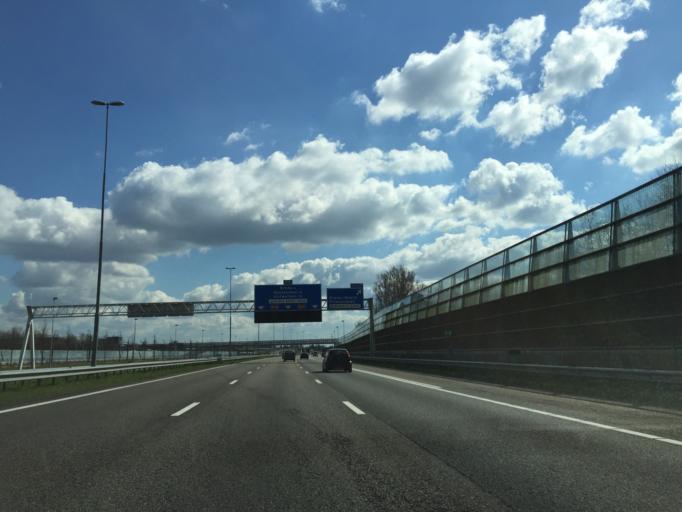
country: NL
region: North Brabant
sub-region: Gemeente Breda
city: Breda
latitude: 51.6089
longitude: 4.7178
